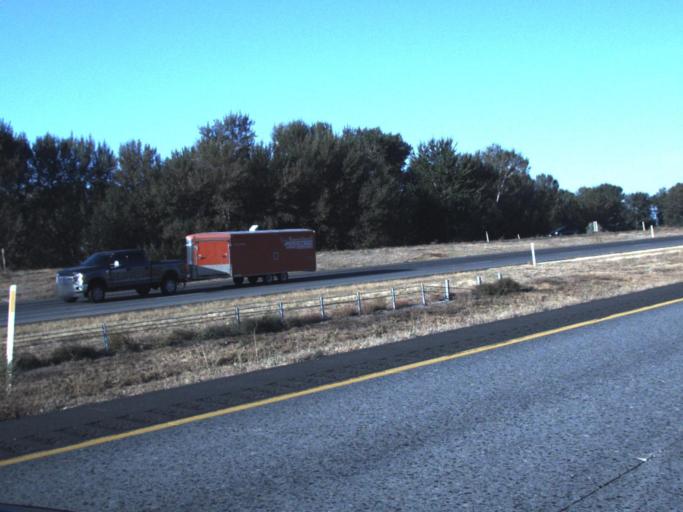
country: US
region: Washington
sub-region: Yakima County
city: Zillah
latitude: 46.4040
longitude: -120.2796
